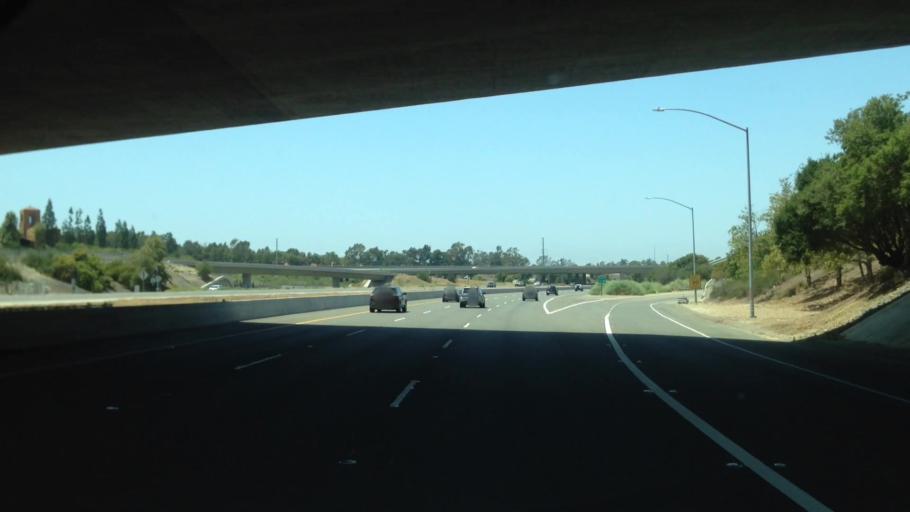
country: US
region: California
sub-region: Orange County
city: San Joaquin Hills
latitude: 33.6377
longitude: -117.8559
